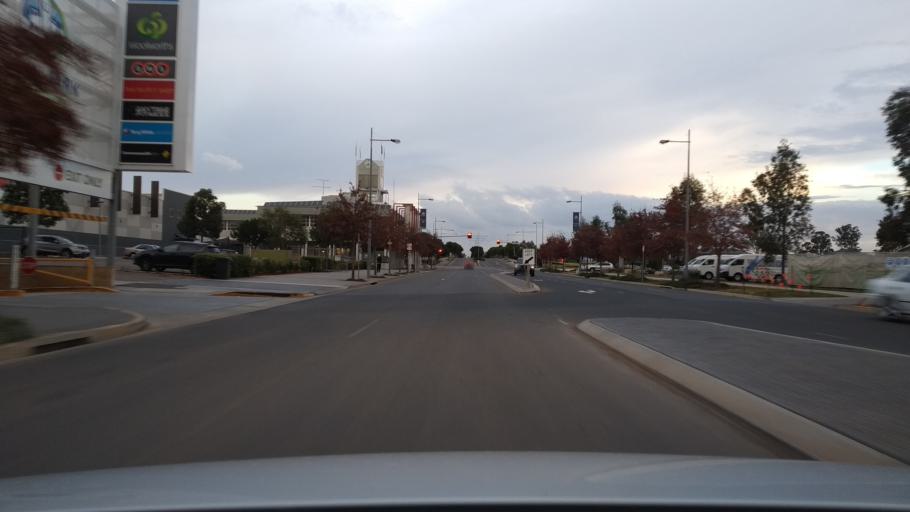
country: AU
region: New South Wales
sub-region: Camden
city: Narellan
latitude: -33.9998
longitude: 150.7397
